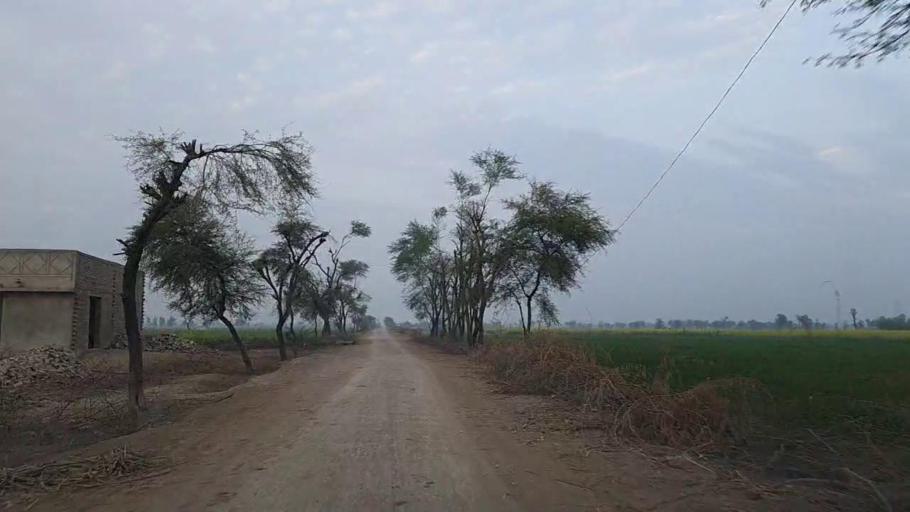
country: PK
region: Sindh
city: Jam Sahib
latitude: 26.3001
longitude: 68.5936
